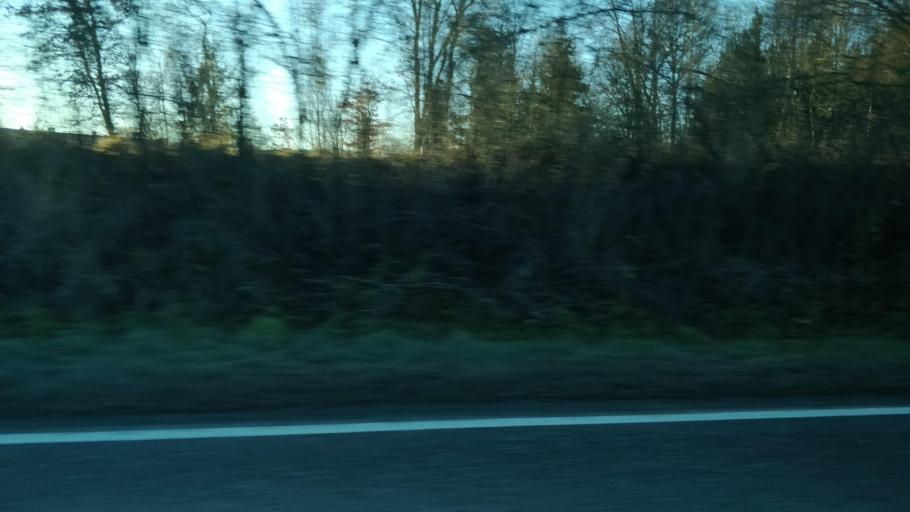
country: DE
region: Bavaria
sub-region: Upper Bavaria
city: Griesstatt
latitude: 47.9897
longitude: 12.1662
